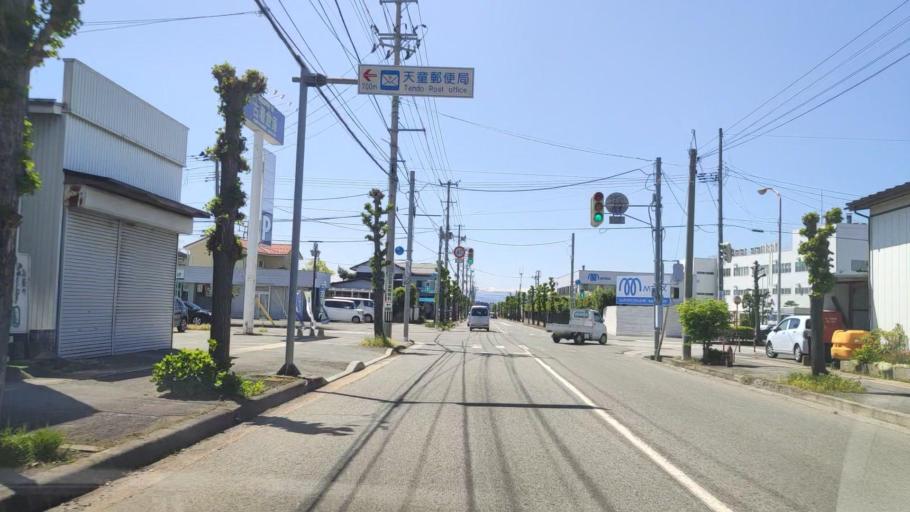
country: JP
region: Yamagata
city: Tendo
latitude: 38.3733
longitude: 140.3786
